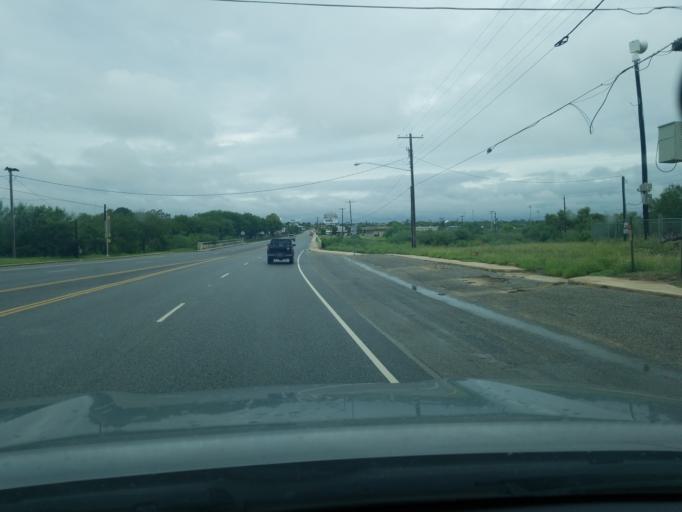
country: US
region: Texas
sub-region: Dimmit County
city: Carrizo Springs
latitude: 28.5206
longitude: -99.8493
